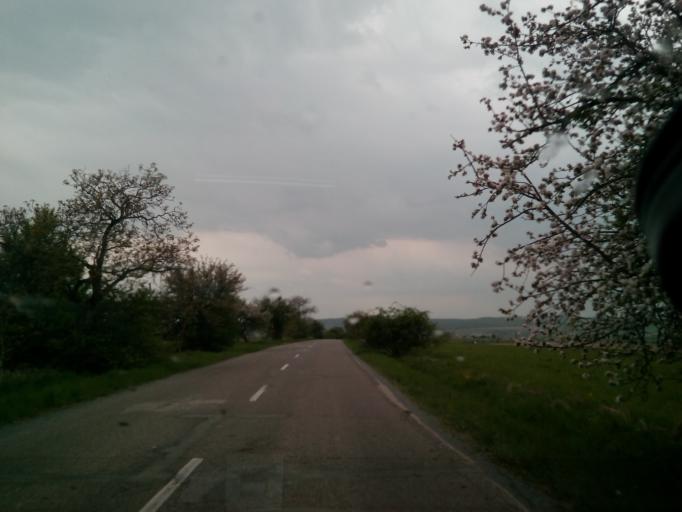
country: SK
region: Kosicky
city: Secovce
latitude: 48.7508
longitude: 21.4616
